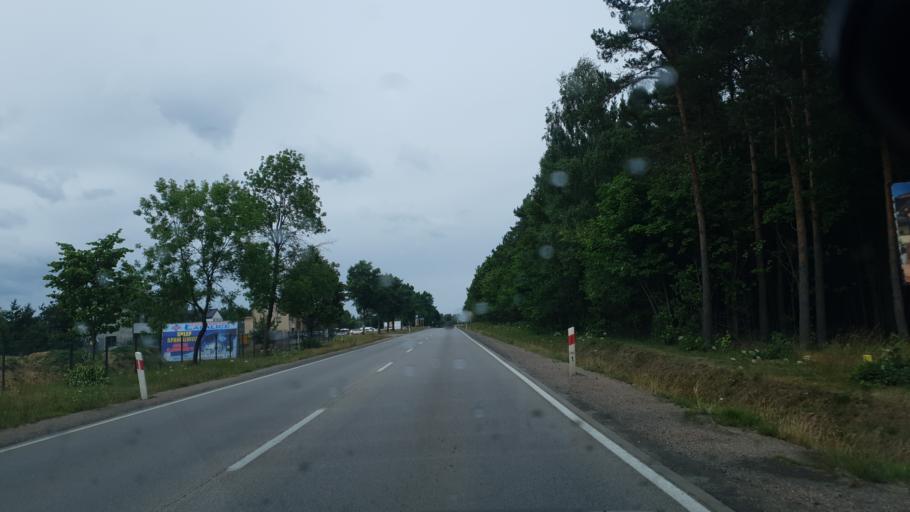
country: PL
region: Pomeranian Voivodeship
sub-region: Powiat kartuski
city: Banino
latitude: 54.3973
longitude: 18.3580
